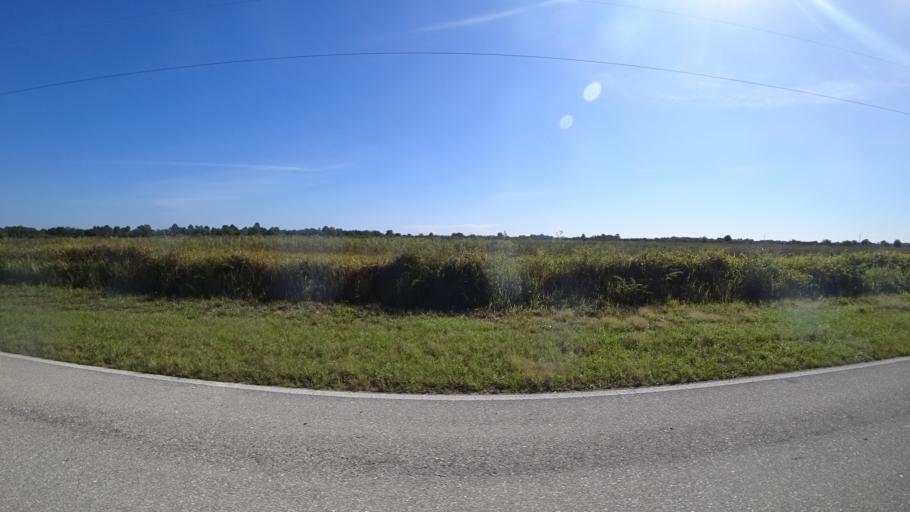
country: US
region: Florida
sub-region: Hillsborough County
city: Wimauma
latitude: 27.6094
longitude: -82.2927
